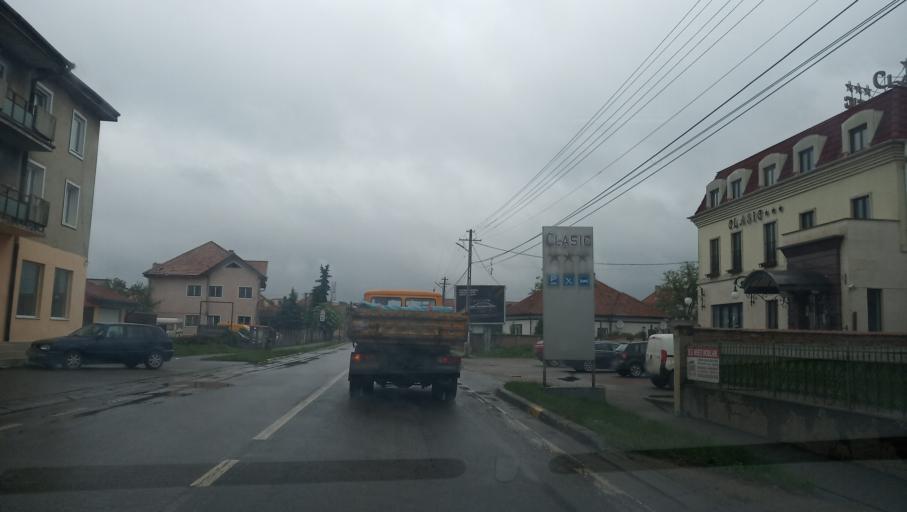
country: RO
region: Alba
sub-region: Municipiul Sebes
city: Sebes
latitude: 45.9528
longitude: 23.5807
